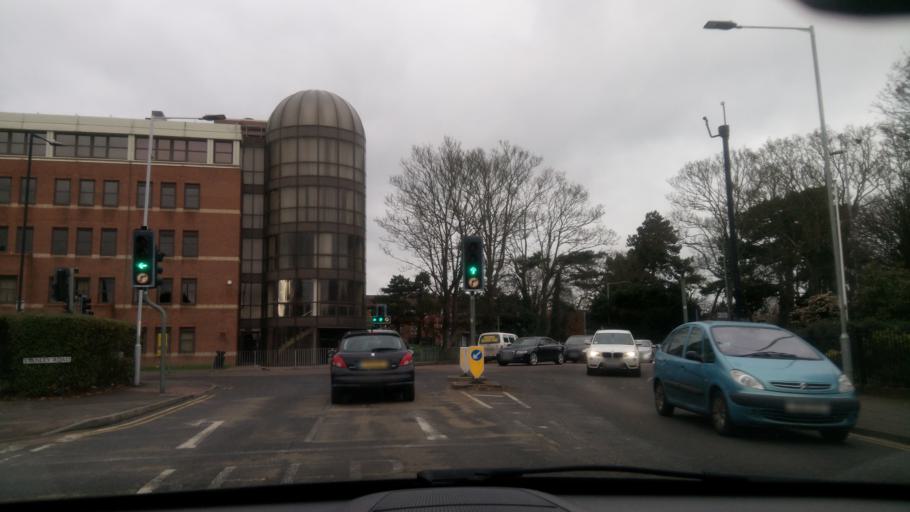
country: GB
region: England
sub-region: Peterborough
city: Peterborough
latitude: 52.5787
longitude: -0.2386
